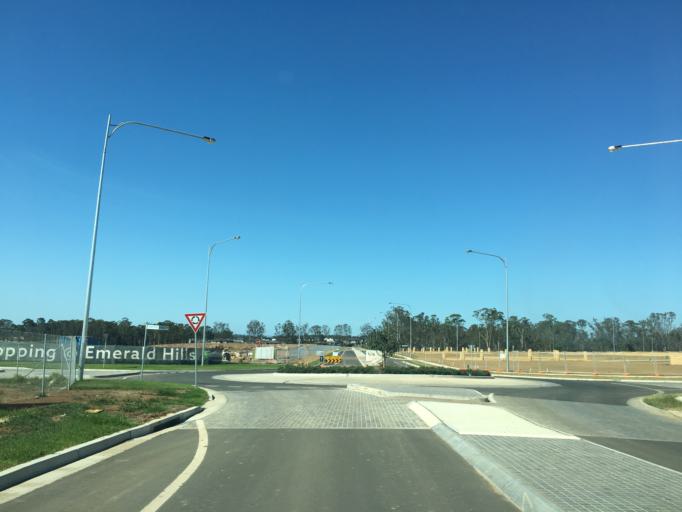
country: AU
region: New South Wales
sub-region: Campbelltown Municipality
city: Denham Court
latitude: -33.9875
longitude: 150.7969
